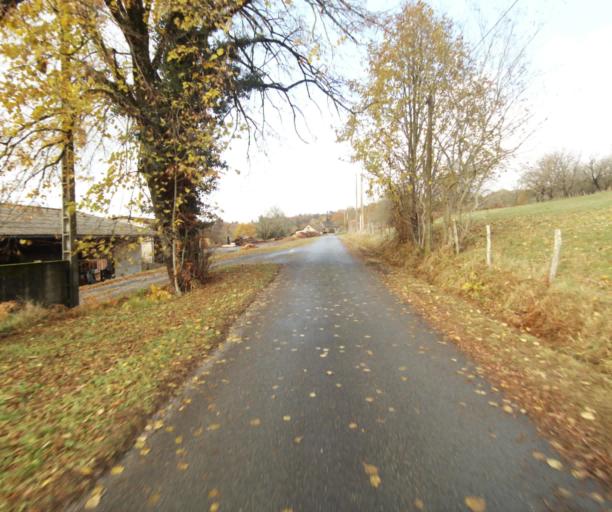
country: FR
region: Limousin
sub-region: Departement de la Correze
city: Cornil
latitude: 45.2194
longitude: 1.6613
